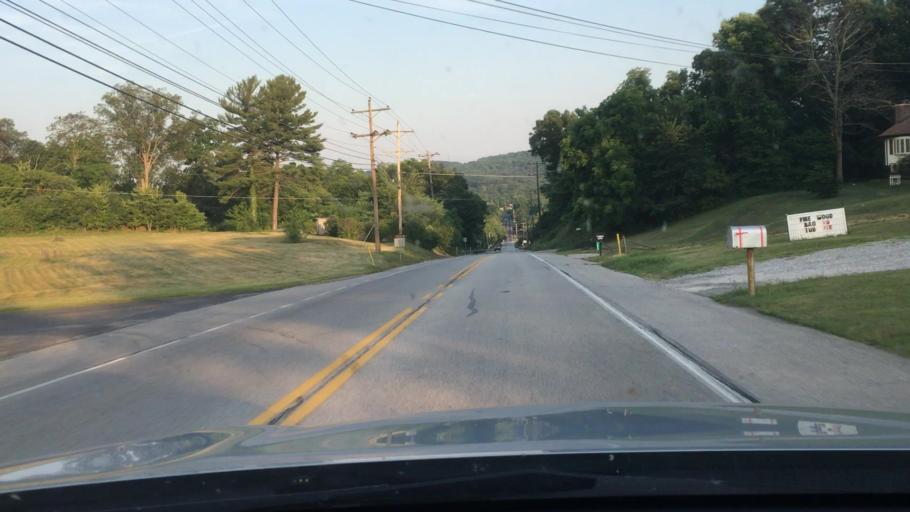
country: US
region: Pennsylvania
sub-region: York County
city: Dover
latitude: 40.0487
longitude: -76.9034
